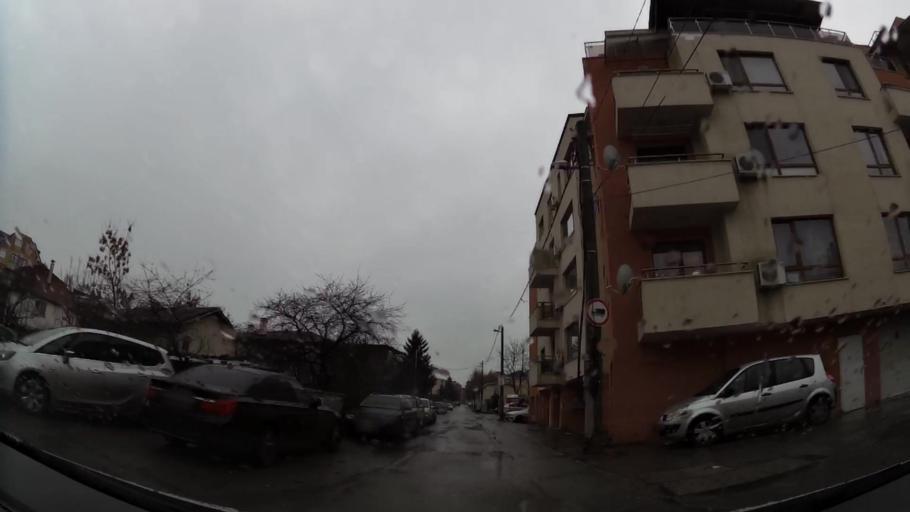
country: BG
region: Sofia-Capital
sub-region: Stolichna Obshtina
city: Sofia
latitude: 42.6482
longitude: 23.3325
